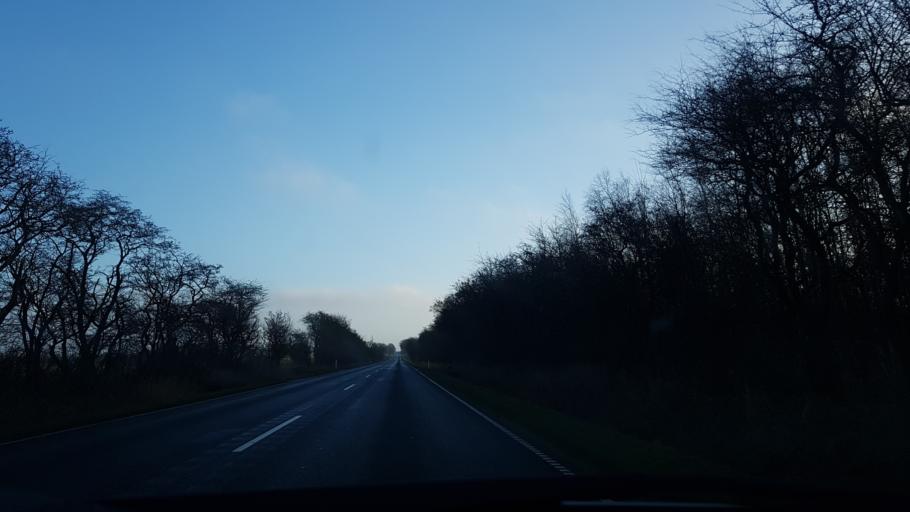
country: DK
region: South Denmark
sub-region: Haderslev Kommune
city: Vojens
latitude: 55.1931
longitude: 9.2082
